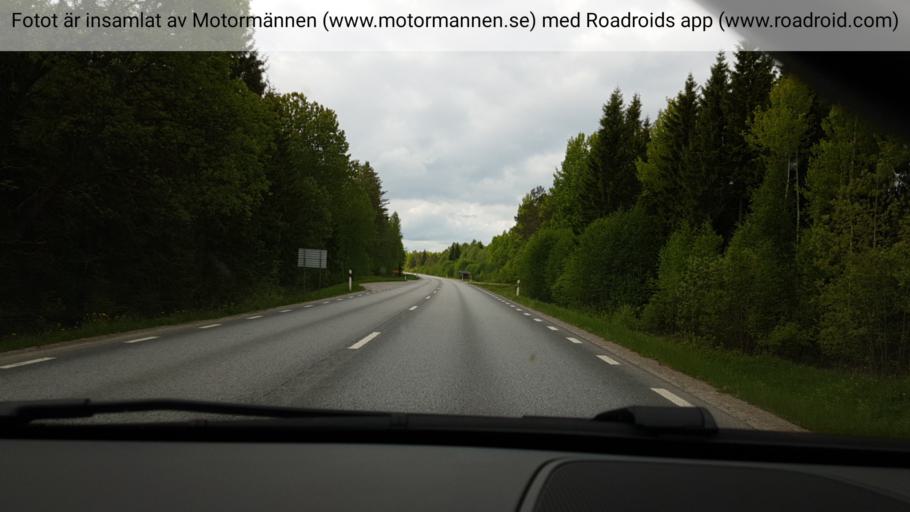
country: SE
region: Uppsala
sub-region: Tierps Kommun
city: Tierp
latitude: 60.3141
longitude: 17.5437
